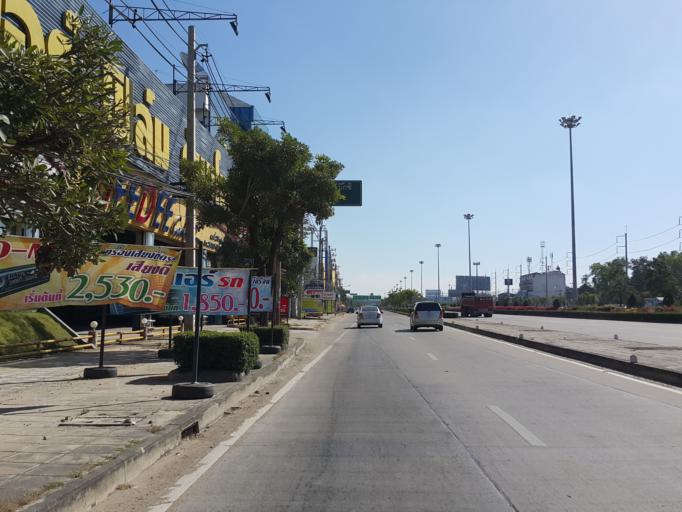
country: TH
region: Chiang Mai
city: Chiang Mai
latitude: 18.7715
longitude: 99.0287
